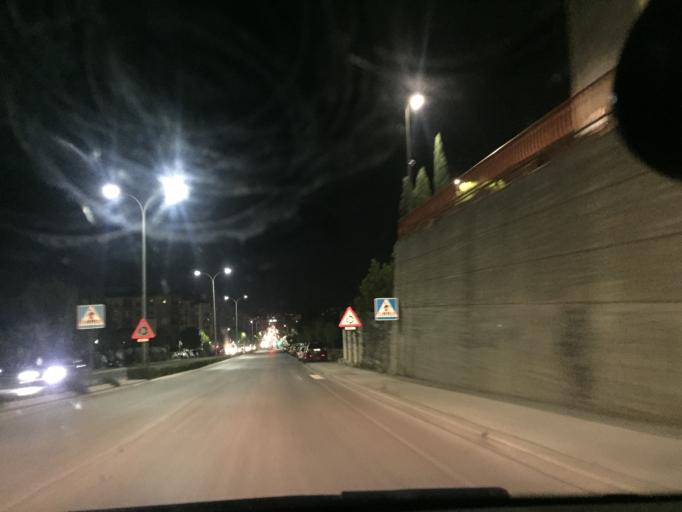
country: ES
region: Andalusia
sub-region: Provincia de Jaen
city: Jaen
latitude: 37.7789
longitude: -3.8115
